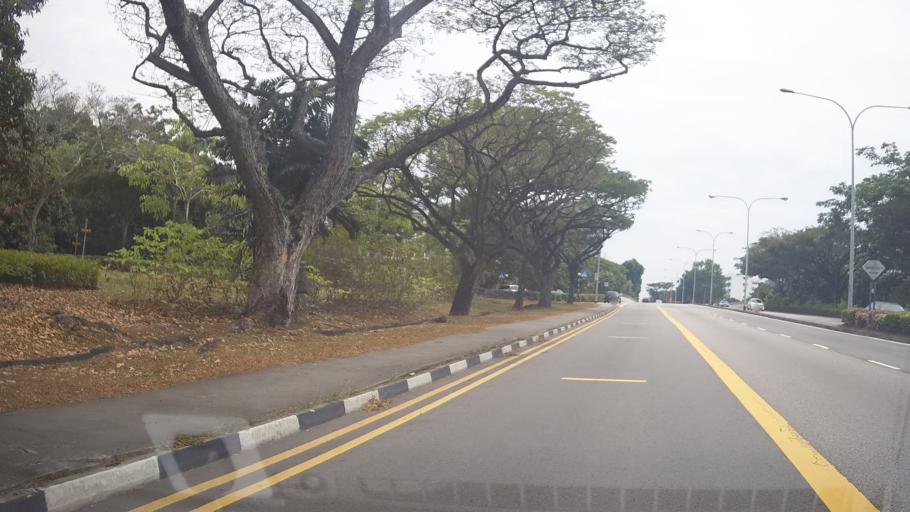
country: SG
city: Singapore
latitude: 1.3430
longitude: 103.9459
